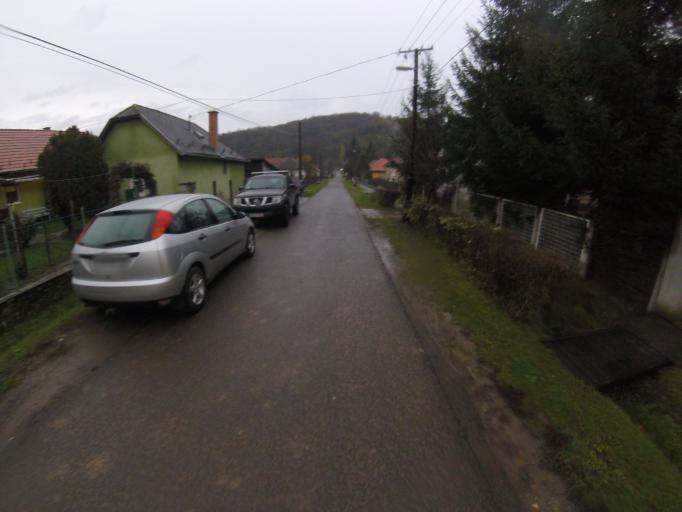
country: HU
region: Nograd
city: Rimoc
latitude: 48.0023
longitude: 19.5090
